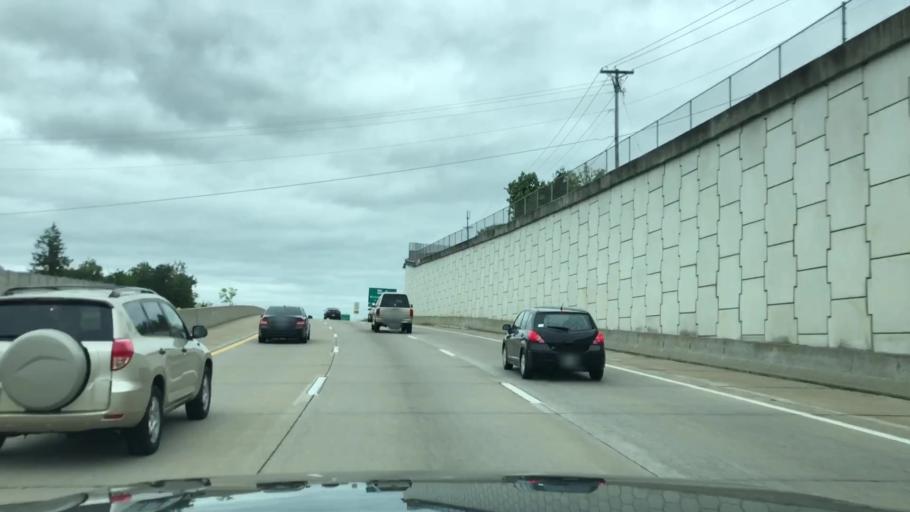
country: US
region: Missouri
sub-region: Saint Louis County
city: Manchester
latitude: 38.6031
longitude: -90.5104
